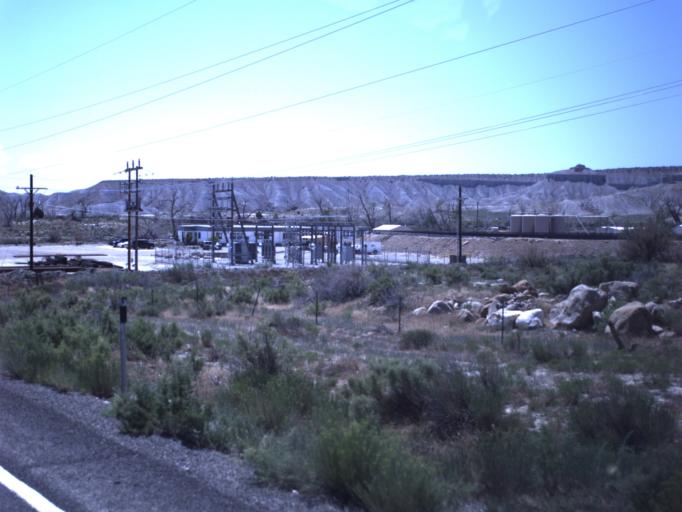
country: US
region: Utah
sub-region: Emery County
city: Orangeville
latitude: 39.2453
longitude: -111.0922
